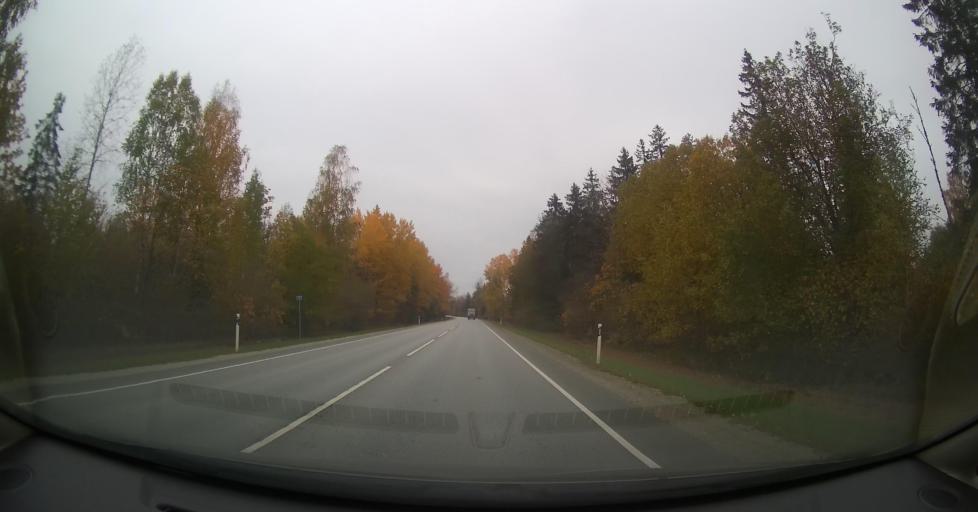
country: EE
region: Harju
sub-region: Nissi vald
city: Riisipere
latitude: 59.1813
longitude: 24.3816
